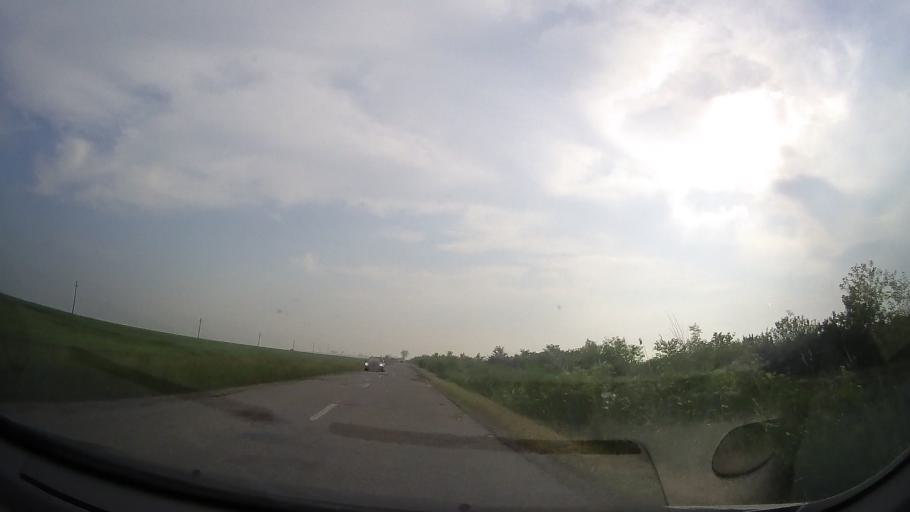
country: RO
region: Timis
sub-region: Comuna Giulvaz
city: Giulvaz
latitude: 45.5777
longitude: 21.0193
